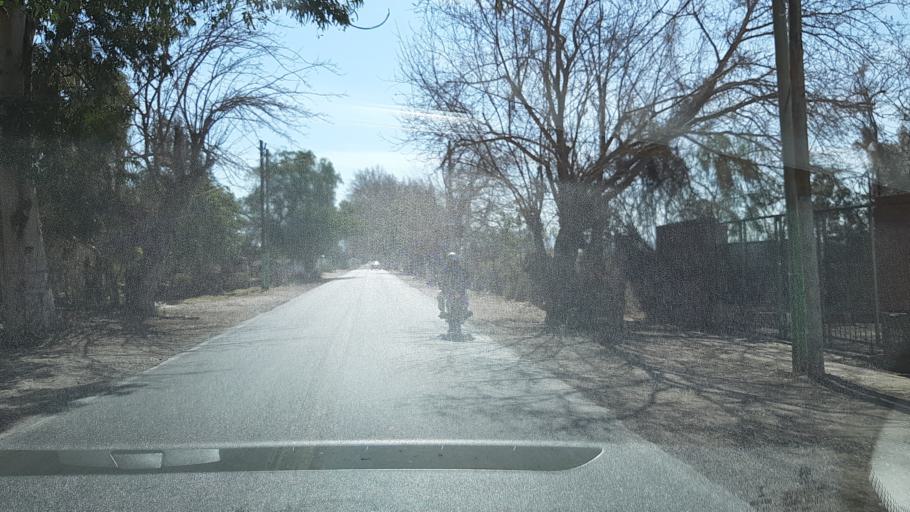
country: AR
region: San Juan
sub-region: Departamento de Rivadavia
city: Rivadavia
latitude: -31.5338
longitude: -68.6180
